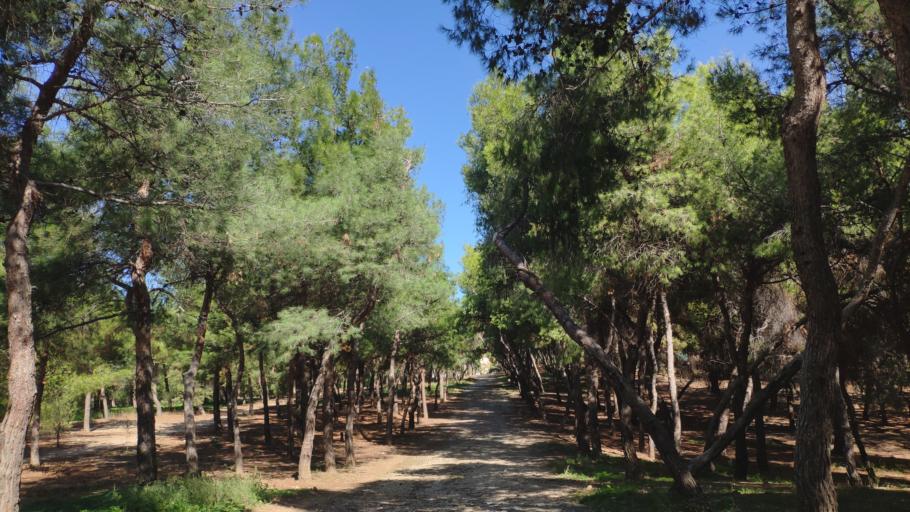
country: GR
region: Attica
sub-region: Nomarchia Athinas
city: Nea Filadelfeia
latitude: 38.0460
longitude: 23.7468
